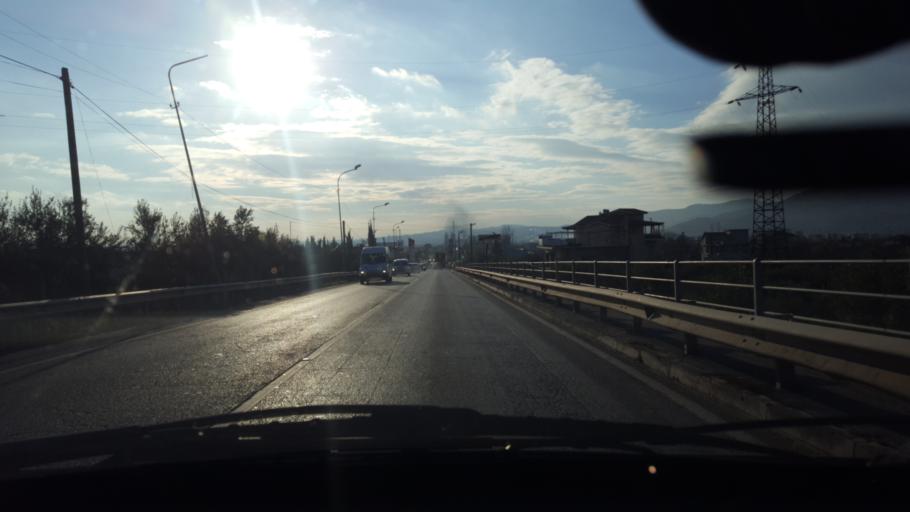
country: AL
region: Elbasan
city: Elbasan
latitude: 41.1047
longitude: 20.0613
